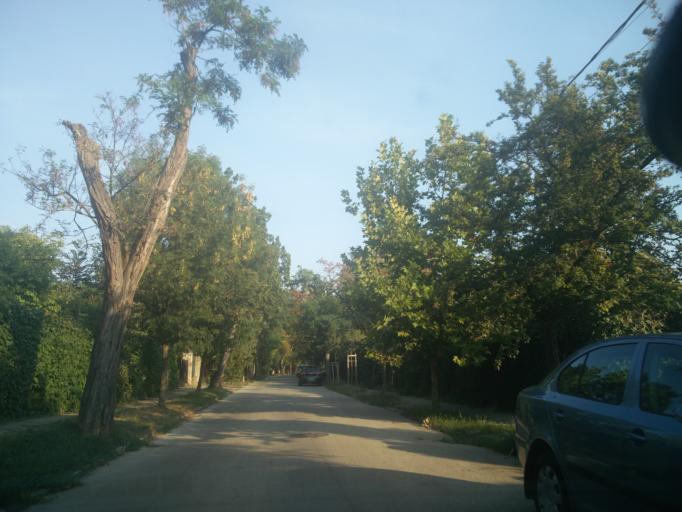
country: HU
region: Budapest
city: Budapest XII. keruelet
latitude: 47.4871
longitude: 19.0146
